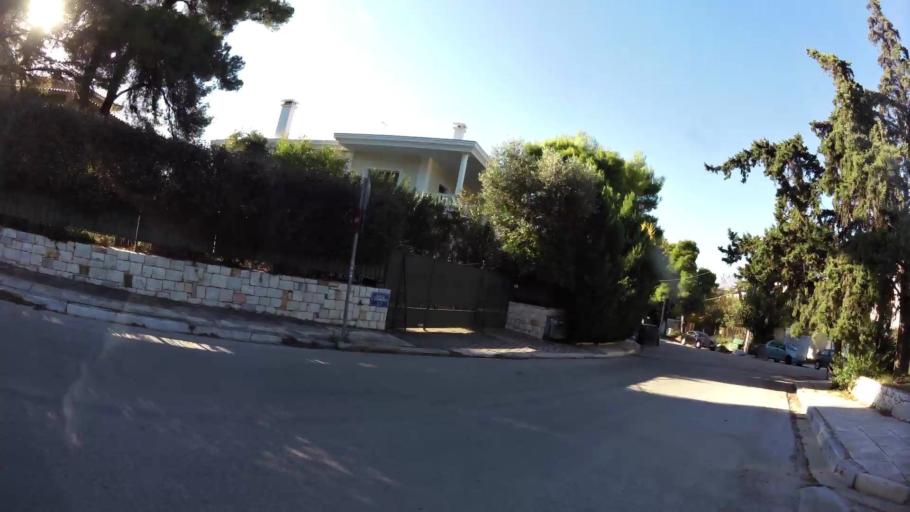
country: GR
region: Attica
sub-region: Nomarchia Athinas
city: Ekali
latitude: 38.1060
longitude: 23.8369
